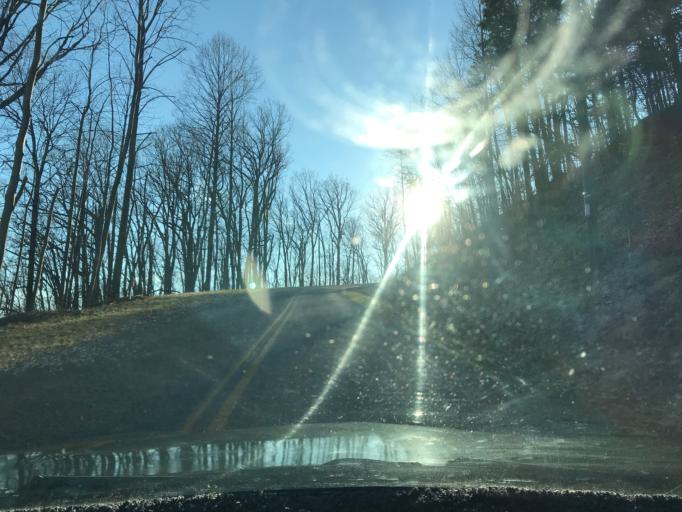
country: US
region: Virginia
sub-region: Botetourt County
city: Buchanan
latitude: 37.4784
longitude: -79.6612
